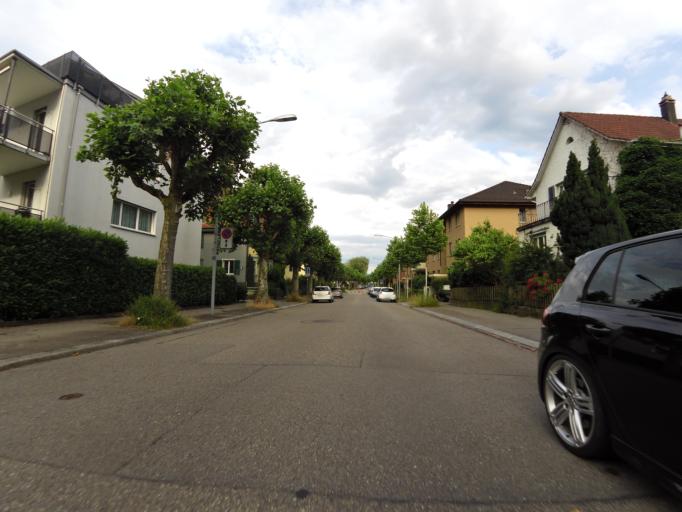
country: CH
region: Zurich
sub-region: Bezirk Zuerich
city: Zuerich (Kreis 9)
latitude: 47.3873
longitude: 8.4772
